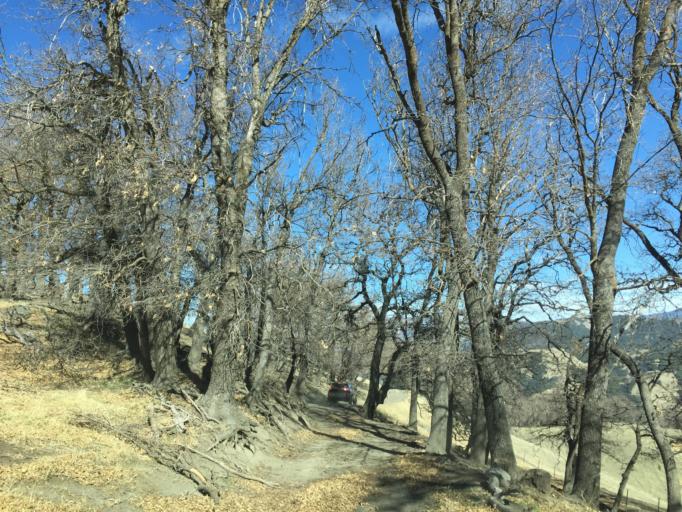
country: US
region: California
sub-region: Kern County
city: Stallion Springs
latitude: 34.9338
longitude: -118.6465
